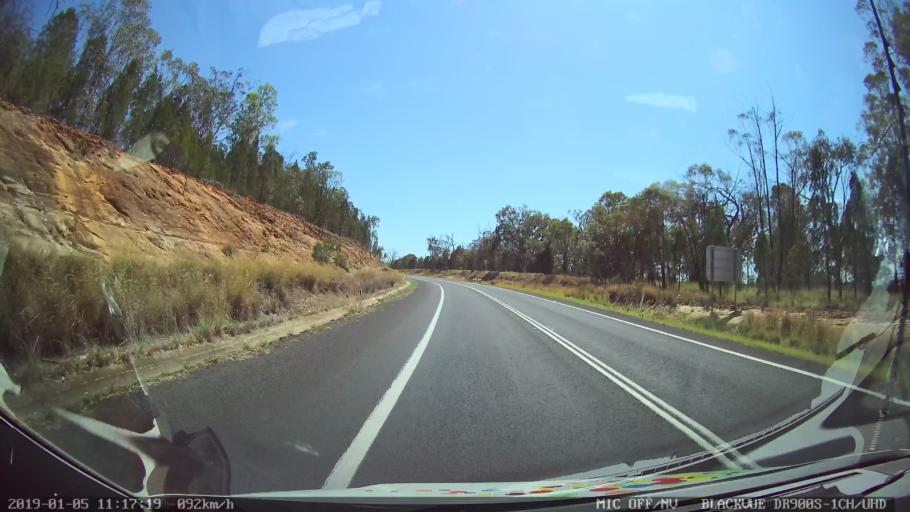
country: AU
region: New South Wales
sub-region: Warrumbungle Shire
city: Coonabarabran
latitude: -31.3279
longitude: 149.3061
